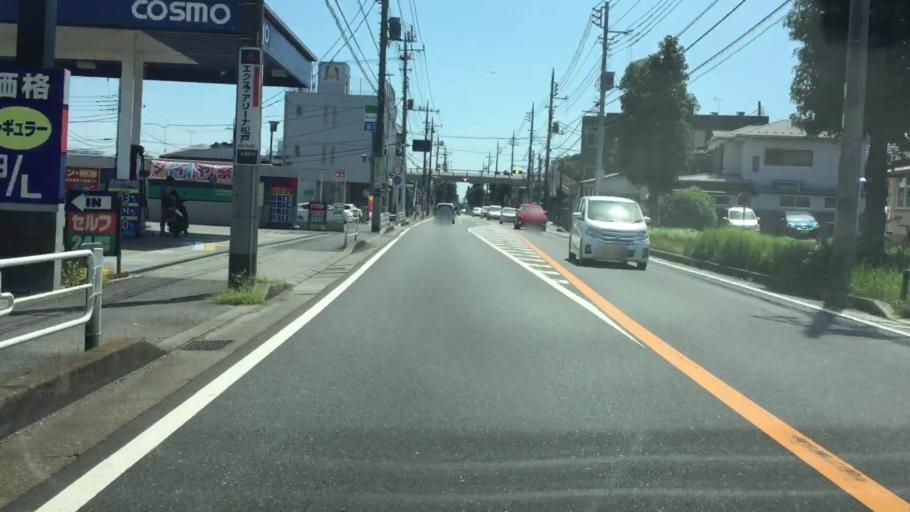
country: JP
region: Chiba
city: Matsudo
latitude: 35.7575
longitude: 139.9368
